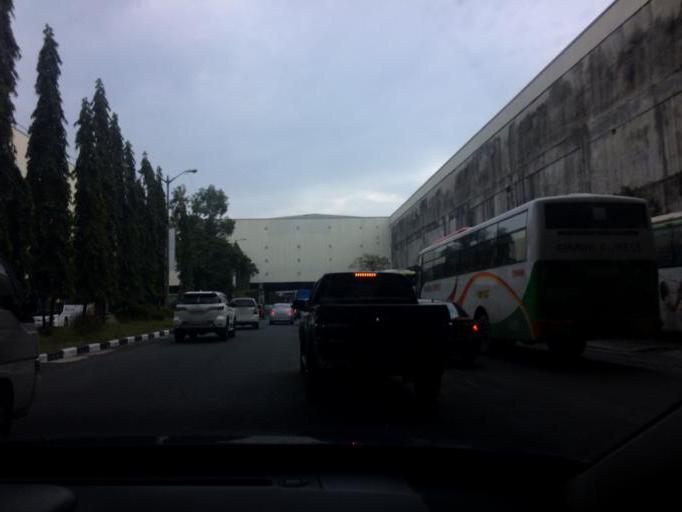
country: PH
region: Metro Manila
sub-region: Makati City
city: Makati City
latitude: 14.5153
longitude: 120.9905
